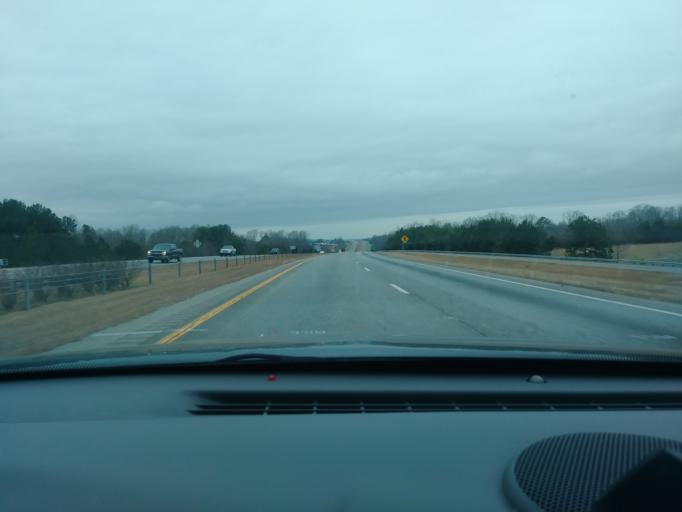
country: US
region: North Carolina
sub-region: Yadkin County
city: Yadkinville
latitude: 36.1165
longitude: -80.7729
